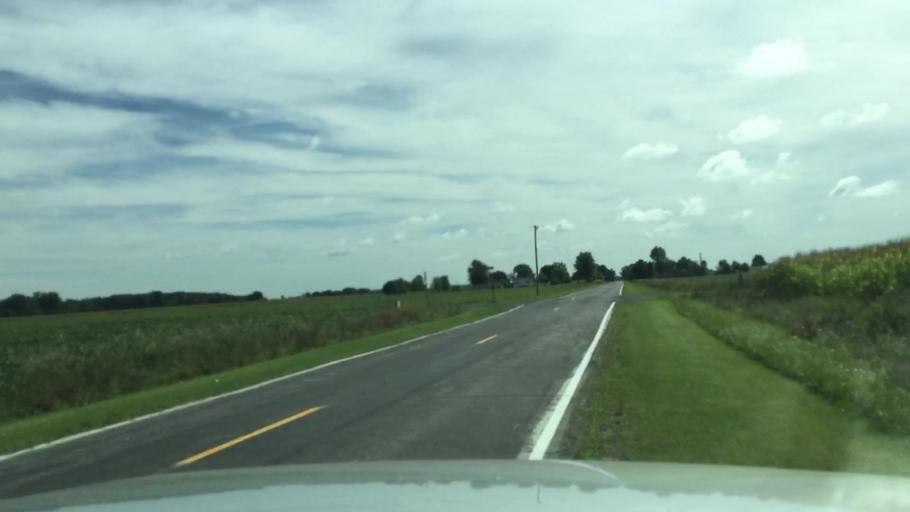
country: US
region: Michigan
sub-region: Saginaw County
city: Chesaning
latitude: 43.1465
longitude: -84.0091
